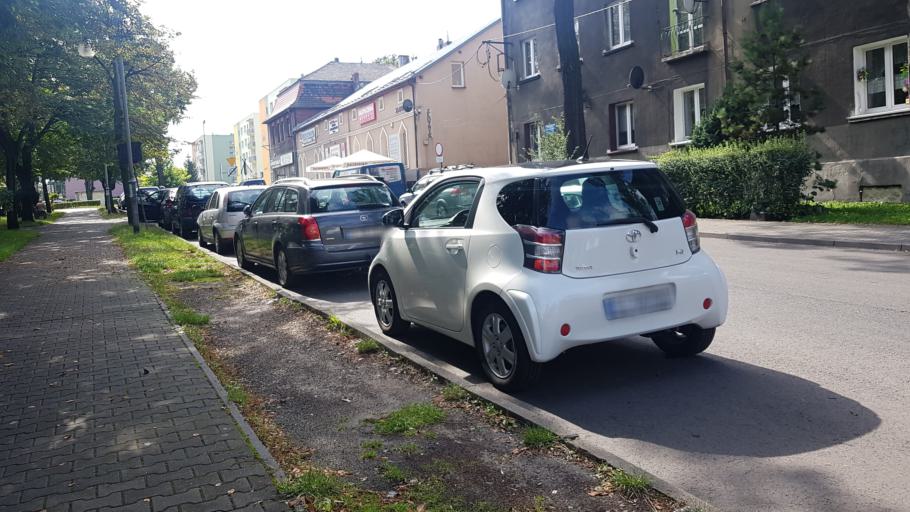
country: PL
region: Silesian Voivodeship
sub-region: Swietochlowice
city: Swietochlowice
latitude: 50.3143
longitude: 18.8855
